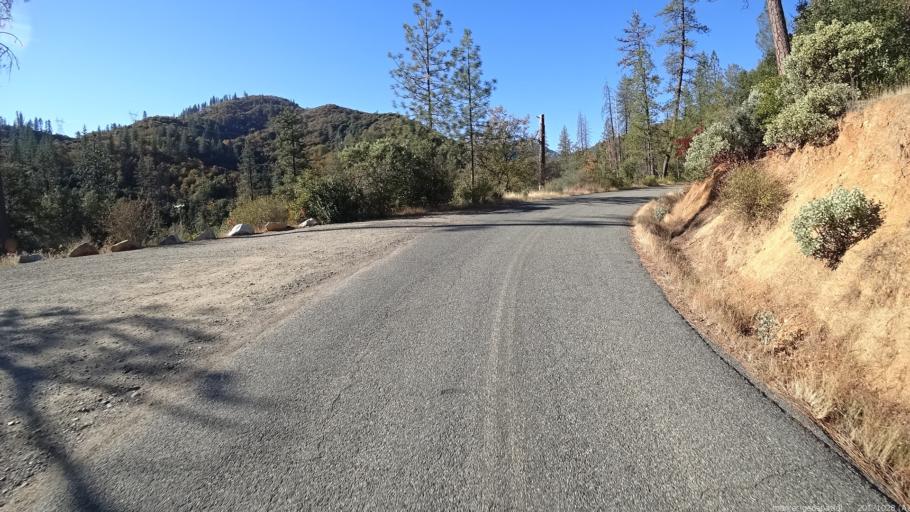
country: US
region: California
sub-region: Trinity County
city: Lewiston
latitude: 40.6677
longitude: -122.6471
